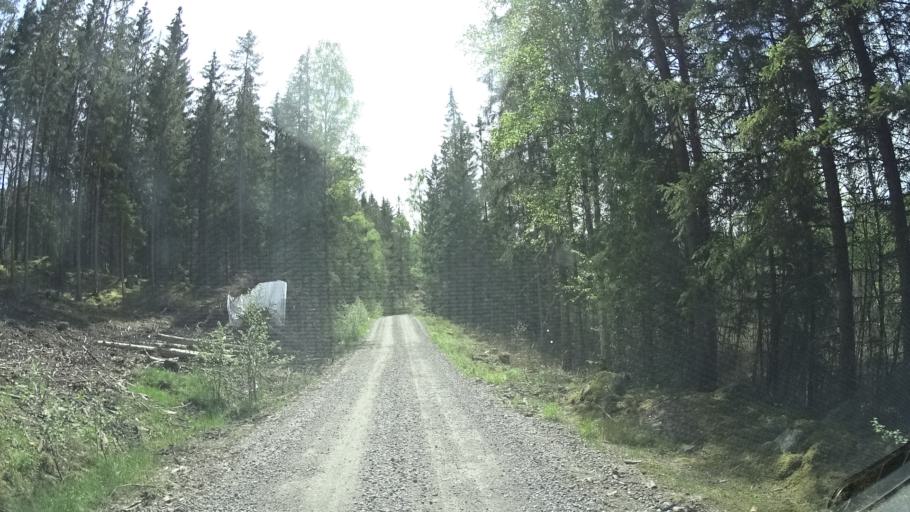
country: SE
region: OEstergoetland
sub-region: Finspangs Kommun
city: Finspang
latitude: 58.7882
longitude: 15.8458
